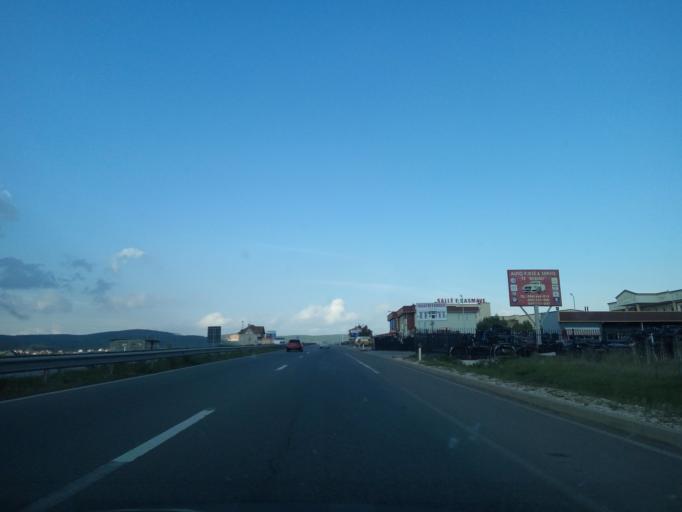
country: XK
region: Pristina
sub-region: Komuna e Drenasit
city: Glogovac
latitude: 42.5944
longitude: 20.9268
